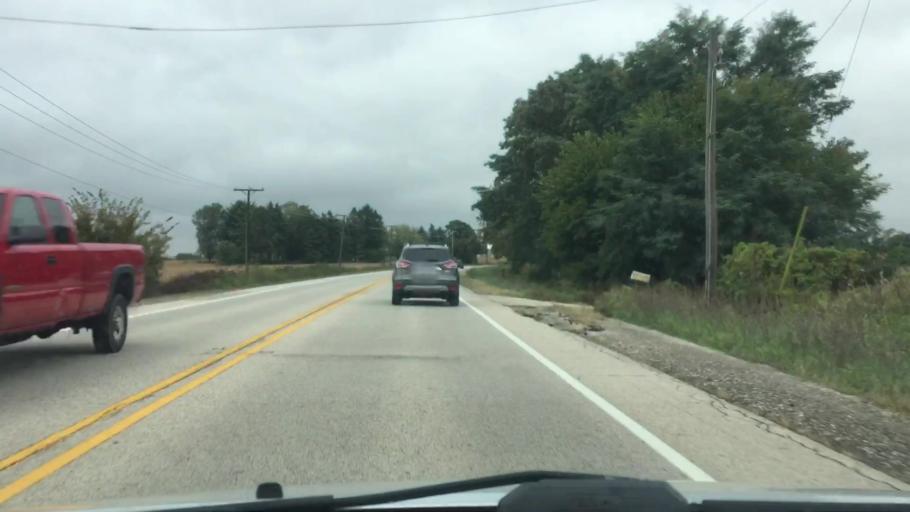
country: US
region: Illinois
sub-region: McHenry County
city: McCullom Lake
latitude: 42.3878
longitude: -88.2832
